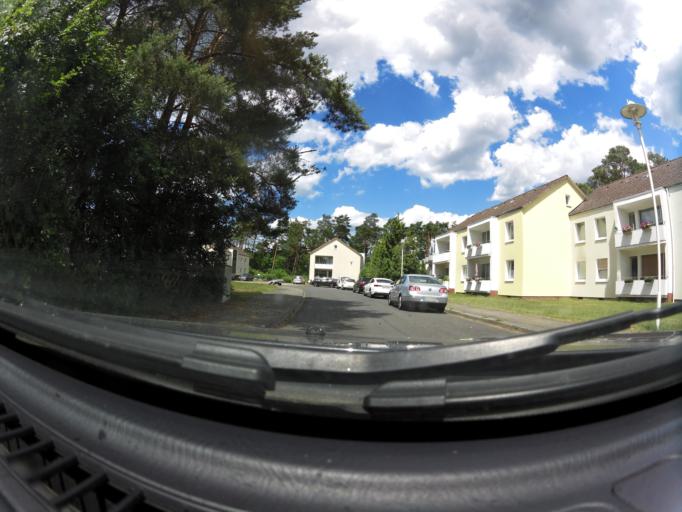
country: DE
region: Lower Saxony
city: Celle
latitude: 52.6343
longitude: 10.0504
